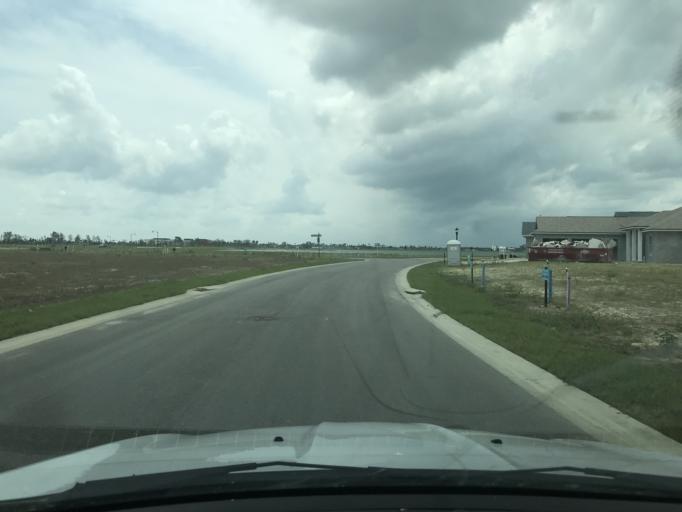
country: US
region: Florida
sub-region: Lee County
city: Olga
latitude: 26.7892
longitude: -81.7377
